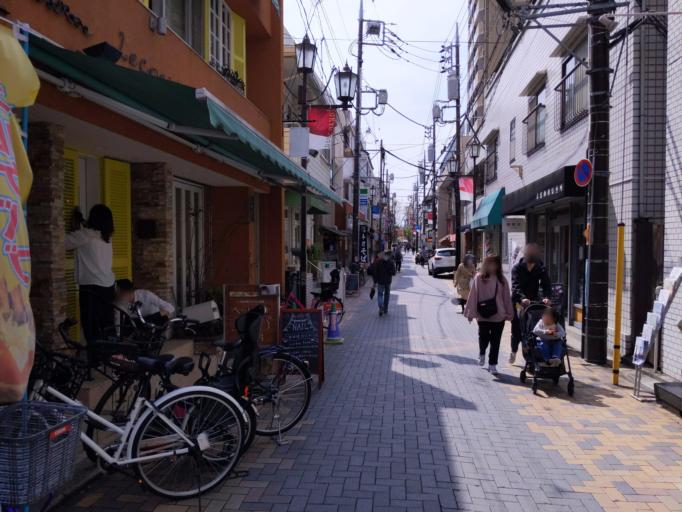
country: JP
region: Saitama
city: Yono
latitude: 35.8718
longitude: 139.6435
